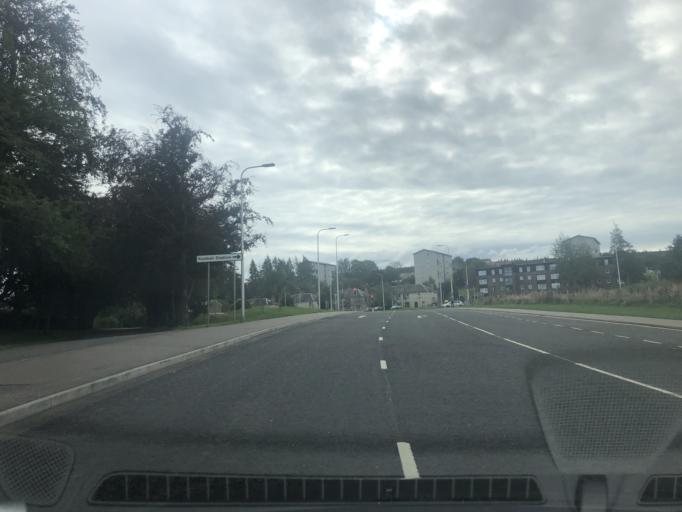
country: GB
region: Scotland
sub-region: Perth and Kinross
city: Perth
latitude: 56.4089
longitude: -3.4719
